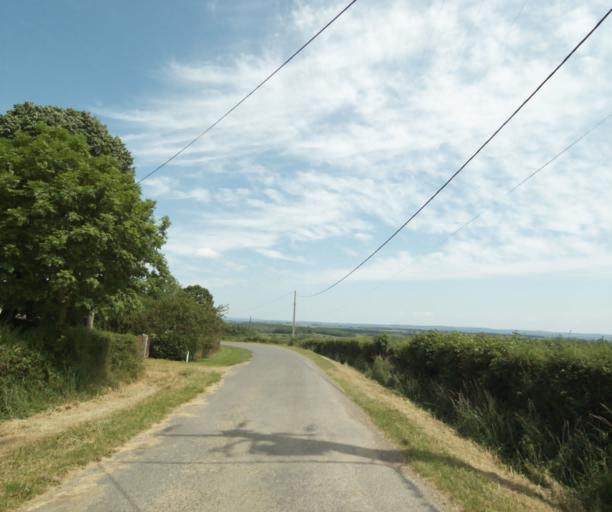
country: FR
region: Bourgogne
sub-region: Departement de Saone-et-Loire
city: Perrecy-les-Forges
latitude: 46.5975
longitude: 4.1481
